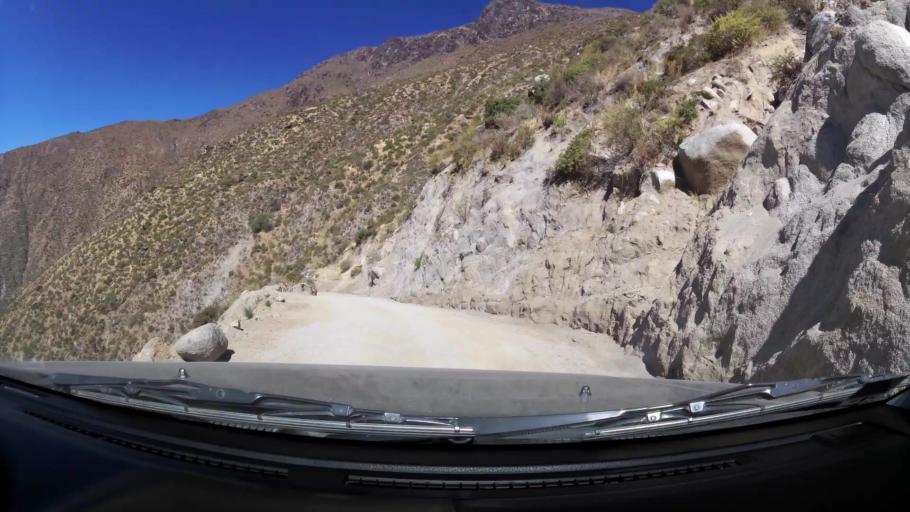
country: PE
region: Huancavelica
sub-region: Huaytara
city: Quito-Arma
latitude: -13.6179
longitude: -75.3503
